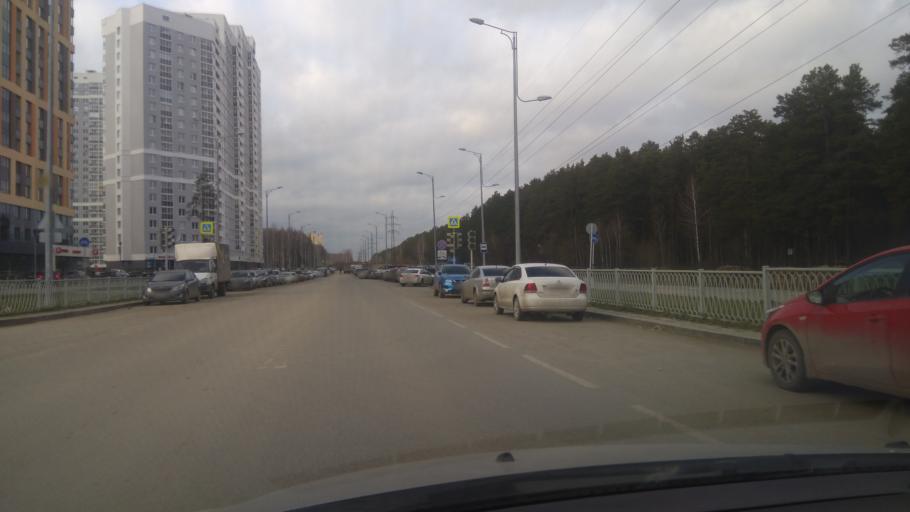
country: RU
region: Sverdlovsk
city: Sovkhoznyy
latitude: 56.7849
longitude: 60.5510
